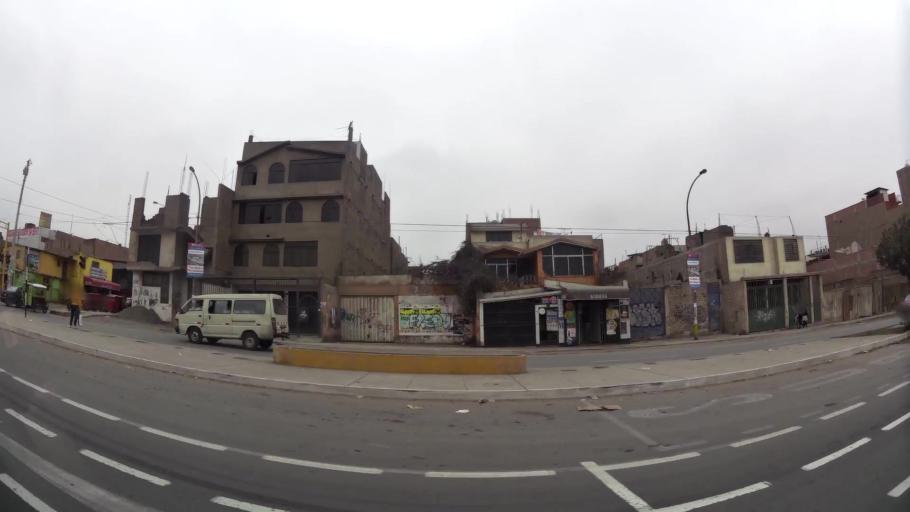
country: PE
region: Lima
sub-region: Lima
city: Vitarte
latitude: -12.0384
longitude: -76.9242
